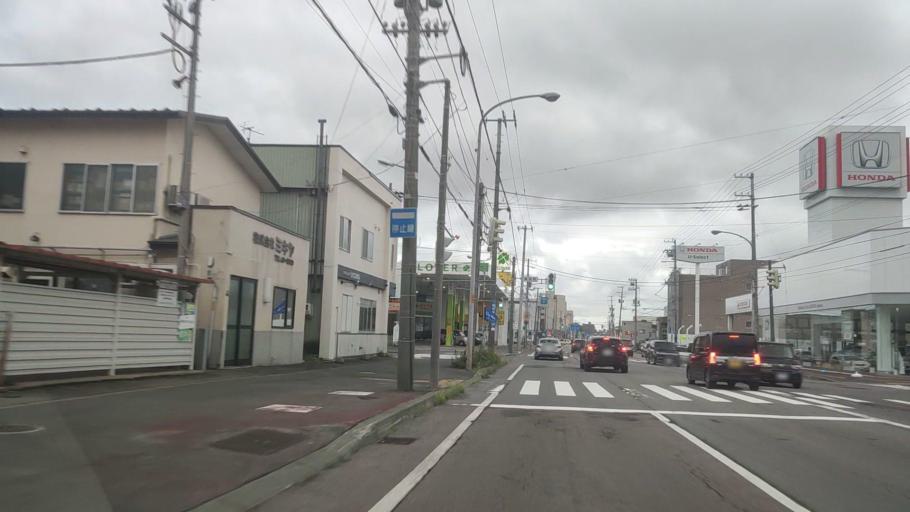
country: JP
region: Hokkaido
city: Hakodate
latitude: 41.7952
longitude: 140.7334
